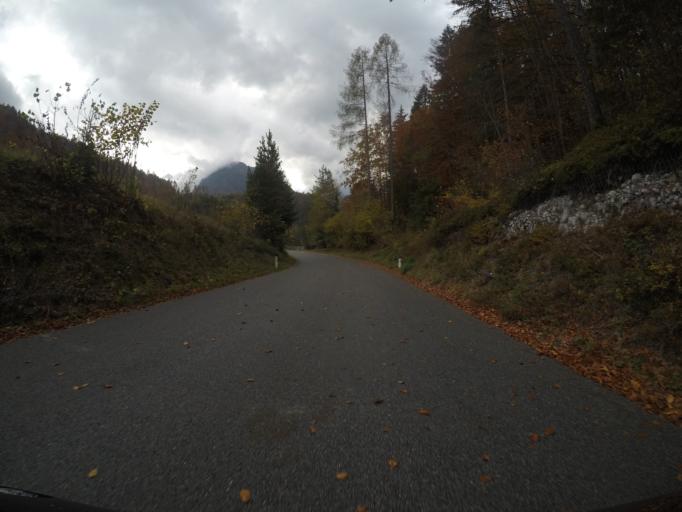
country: SI
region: Kranjska Gora
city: Mojstrana
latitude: 46.4564
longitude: 13.9398
